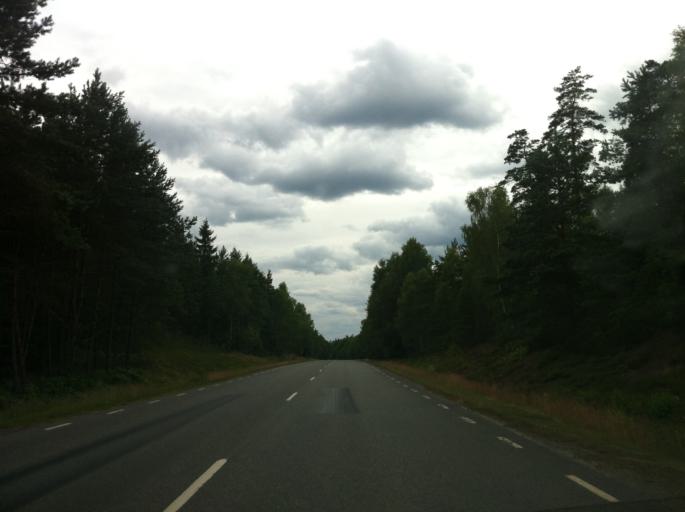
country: SE
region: Skane
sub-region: Osby Kommun
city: Lonsboda
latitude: 56.3818
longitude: 14.2670
